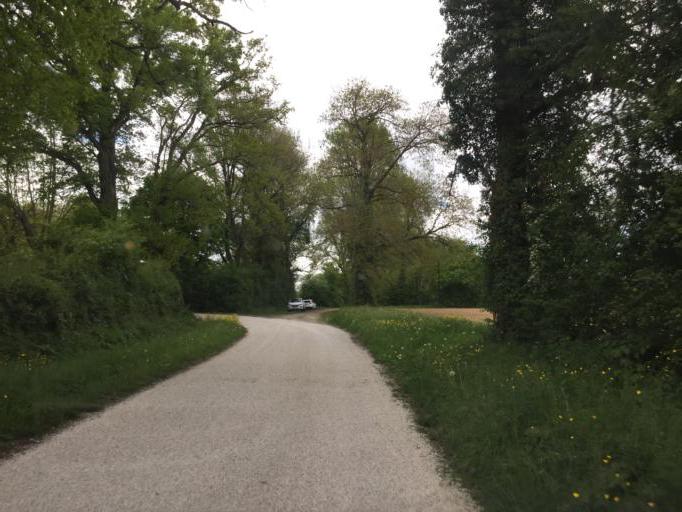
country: FR
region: Rhone-Alpes
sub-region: Departement de l'Ain
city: Tramoyes
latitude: 45.9034
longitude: 4.9779
